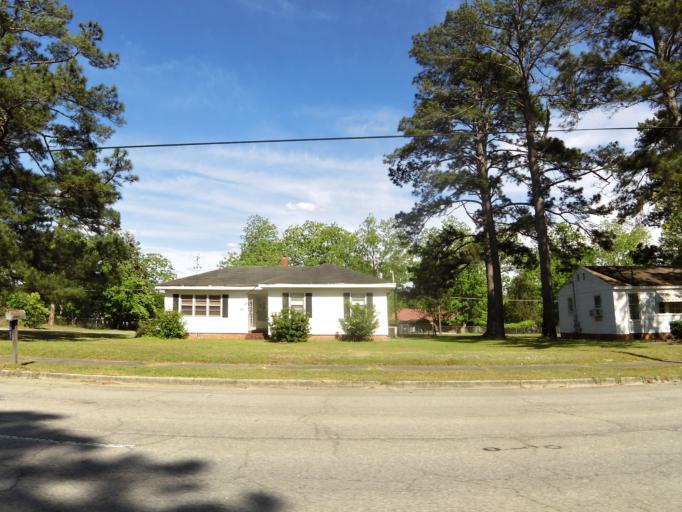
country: US
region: South Carolina
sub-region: Bamberg County
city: Denmark
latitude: 33.3067
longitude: -81.1447
